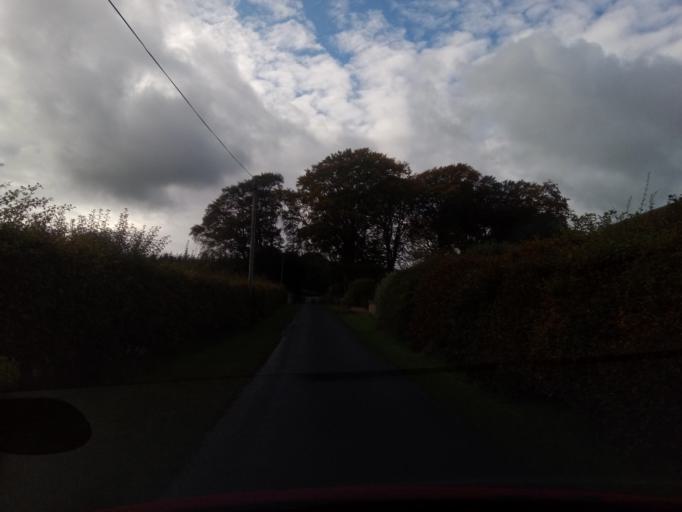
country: GB
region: Scotland
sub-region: The Scottish Borders
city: Galashiels
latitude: 55.6750
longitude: -2.8270
